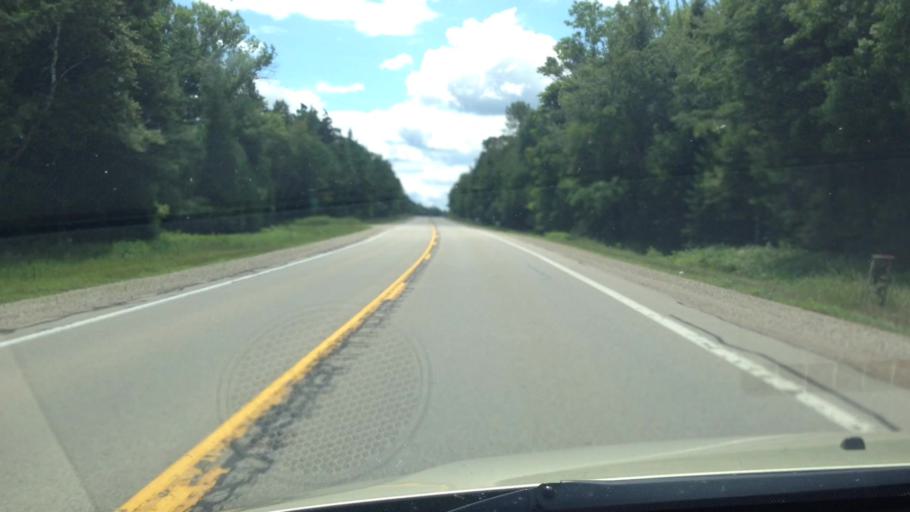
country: US
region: Michigan
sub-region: Menominee County
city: Menominee
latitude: 45.3668
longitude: -87.3958
